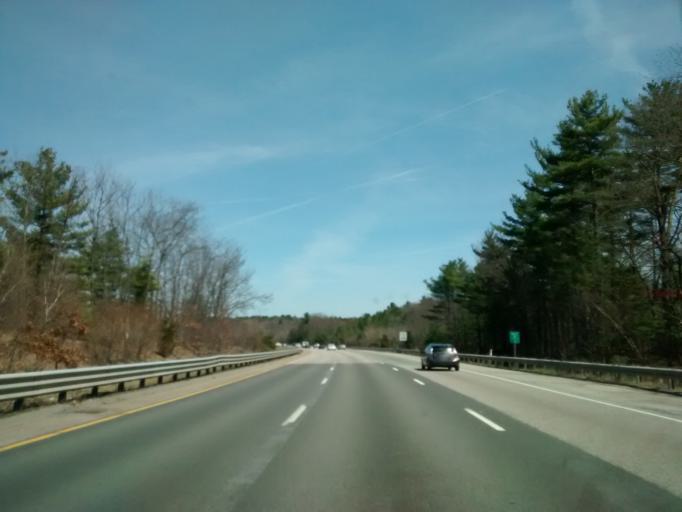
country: US
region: Massachusetts
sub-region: Worcester County
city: Northborough
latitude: 42.3325
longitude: -71.6690
